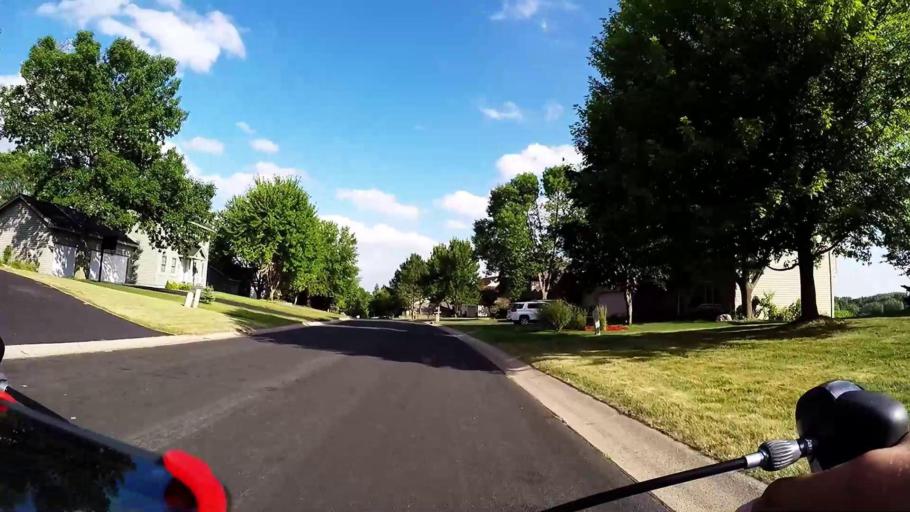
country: US
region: Minnesota
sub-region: Hennepin County
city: Eden Prairie
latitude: 44.8846
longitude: -93.4439
